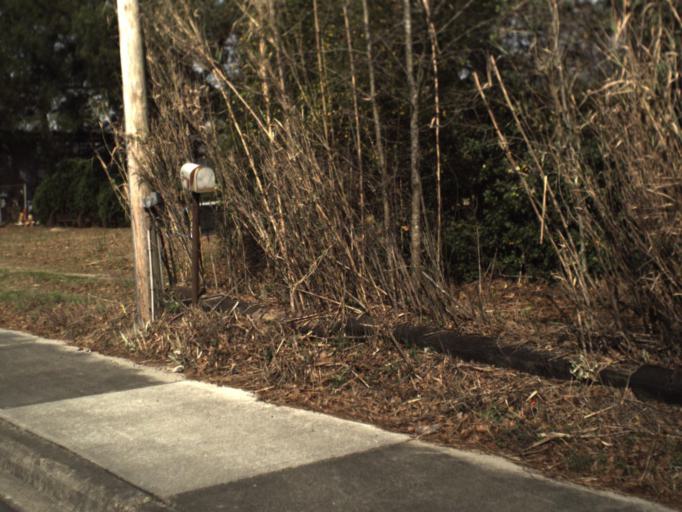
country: US
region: Florida
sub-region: Bay County
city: Youngstown
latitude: 30.3711
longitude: -85.4383
